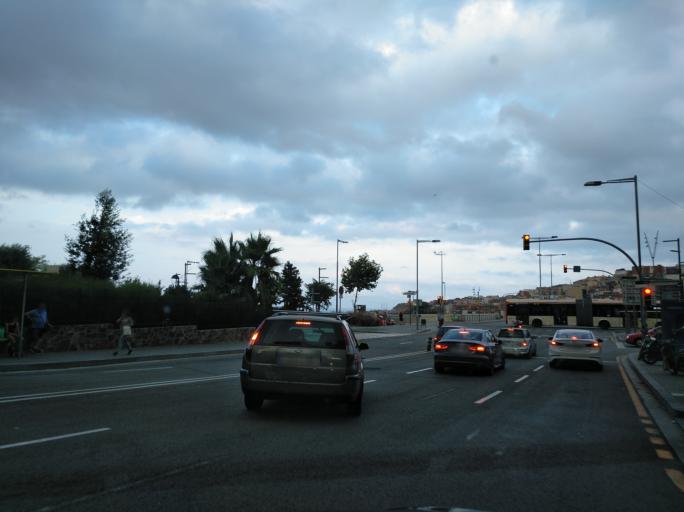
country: ES
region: Catalonia
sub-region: Provincia de Barcelona
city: Sarria-Sant Gervasi
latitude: 41.4250
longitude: 2.1413
